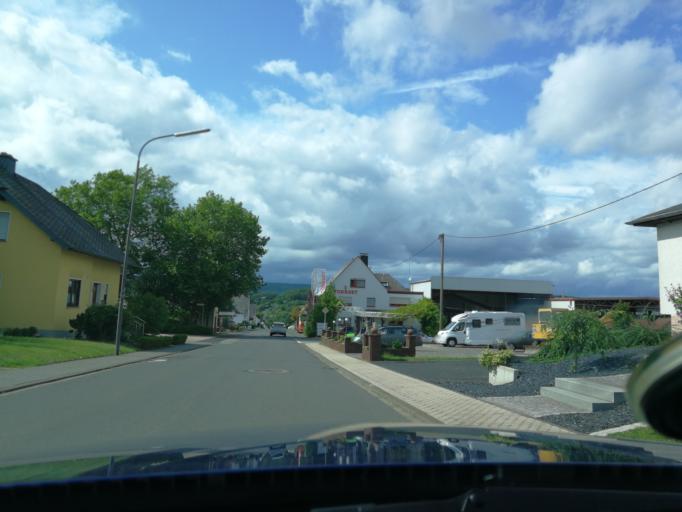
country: DE
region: Rheinland-Pfalz
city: Klausen
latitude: 49.9095
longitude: 6.8806
